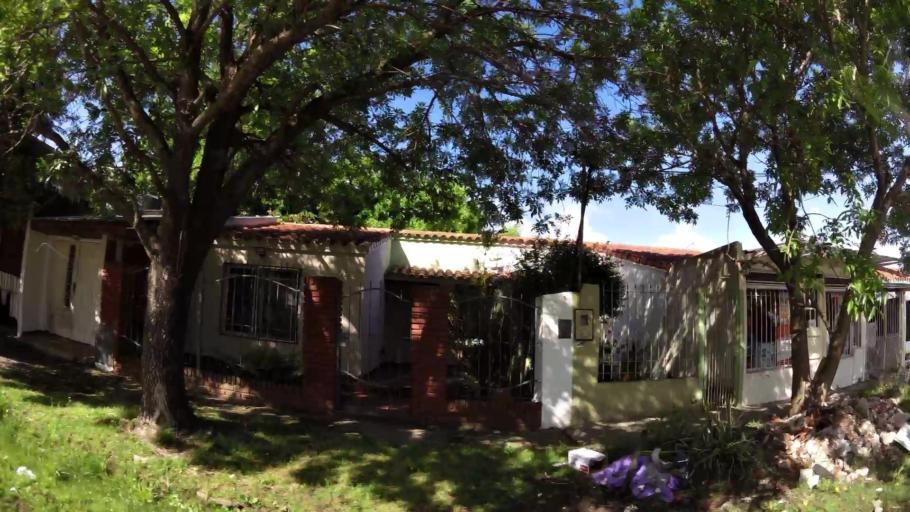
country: AR
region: Buenos Aires
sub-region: Partido de Quilmes
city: Quilmes
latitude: -34.7866
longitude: -58.1511
